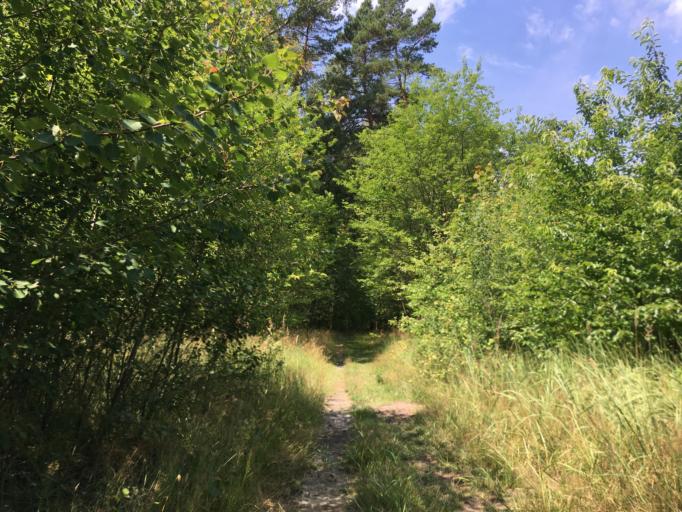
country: DE
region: Brandenburg
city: Glienicke
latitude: 52.6789
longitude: 13.3608
